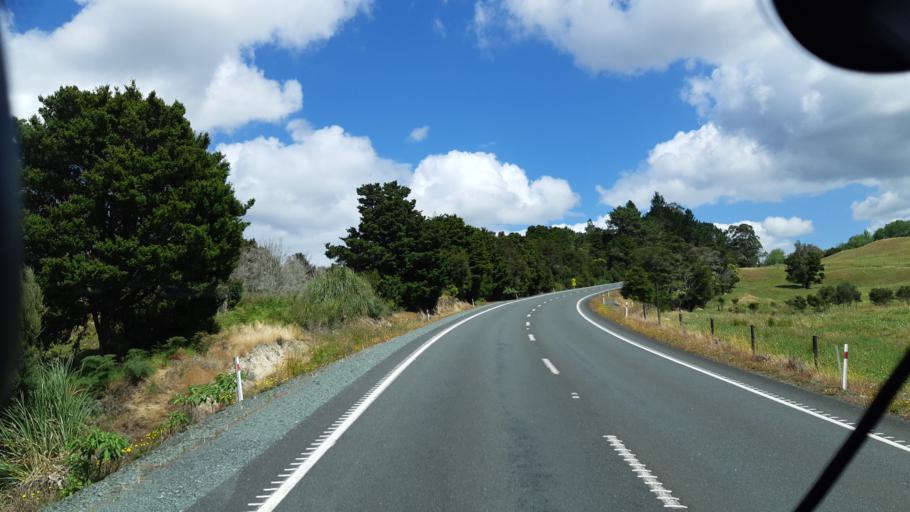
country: NZ
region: Northland
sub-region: Far North District
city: Taipa
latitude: -35.2732
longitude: 173.5664
